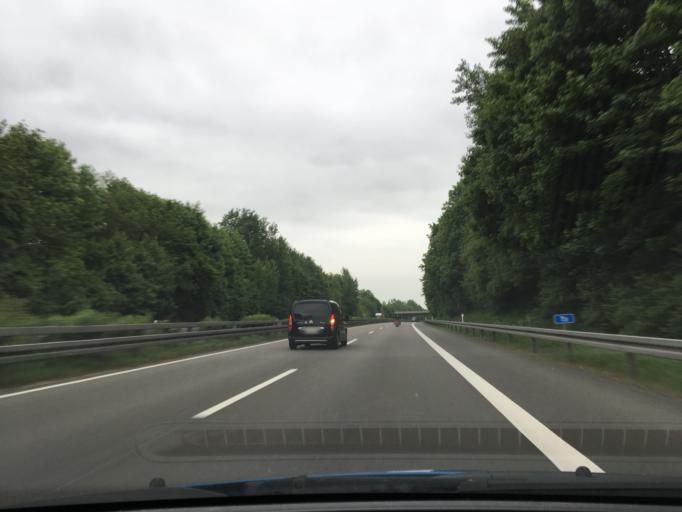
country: DE
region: Lower Saxony
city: Stelle
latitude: 53.3745
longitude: 10.0947
